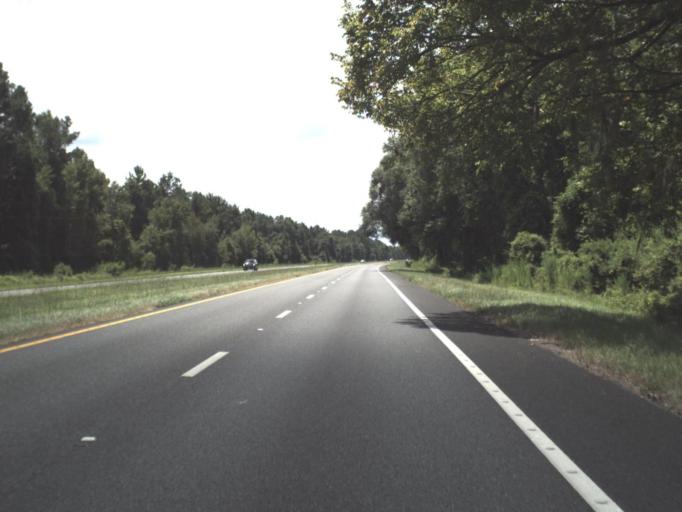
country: US
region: Florida
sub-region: Taylor County
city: Perry
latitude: 30.1906
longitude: -83.6462
